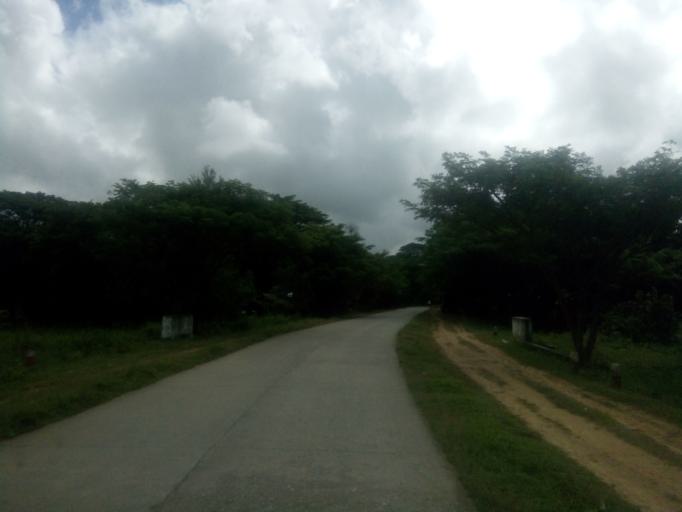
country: MM
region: Bago
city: Nyaunglebin
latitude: 17.9240
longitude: 96.5107
